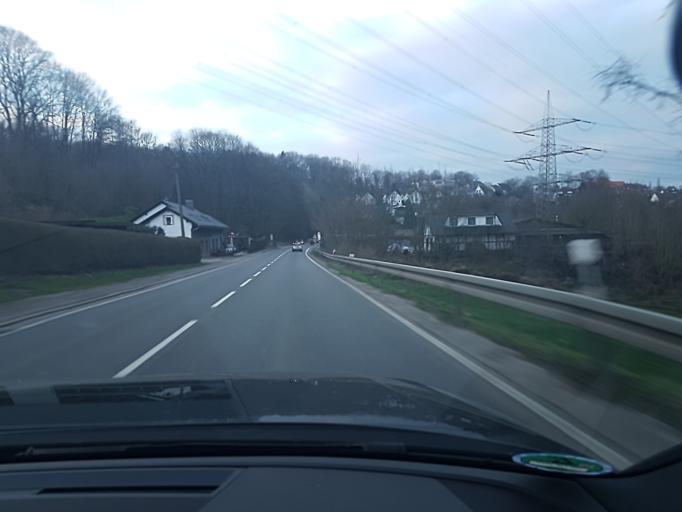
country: DE
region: North Rhine-Westphalia
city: Hattingen
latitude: 51.3854
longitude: 7.1918
